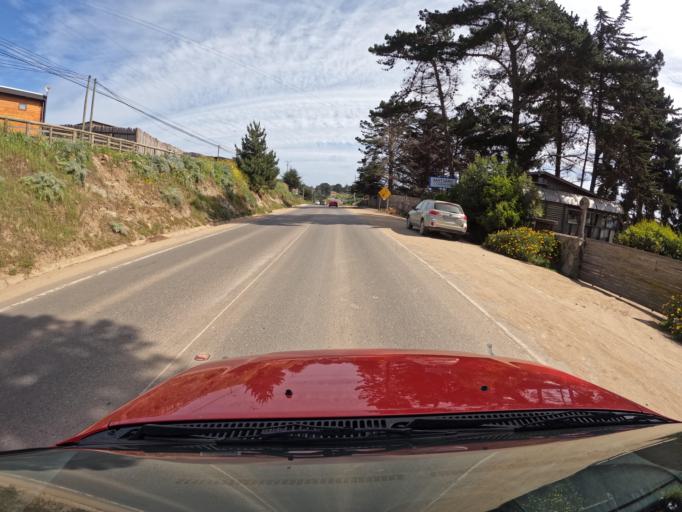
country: CL
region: O'Higgins
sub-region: Provincia de Colchagua
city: Santa Cruz
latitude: -34.4277
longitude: -72.0317
